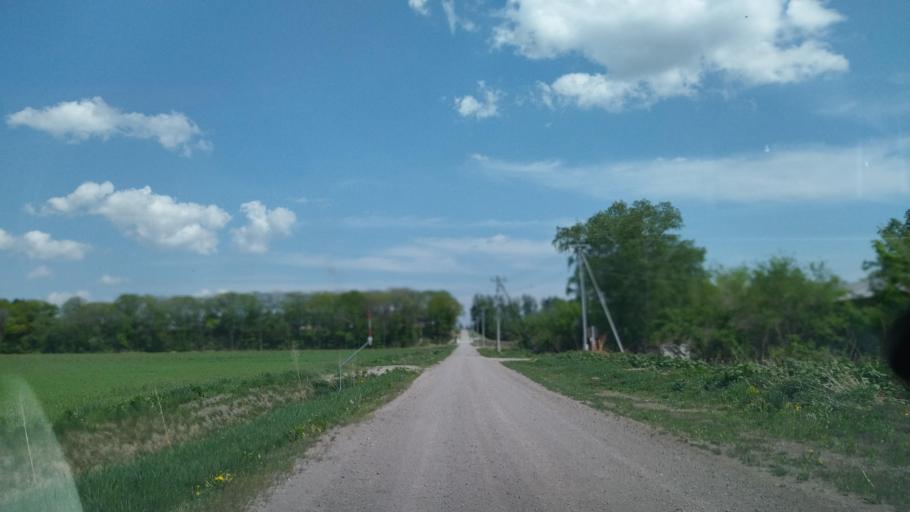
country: JP
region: Hokkaido
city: Otofuke
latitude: 43.1323
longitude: 143.2182
